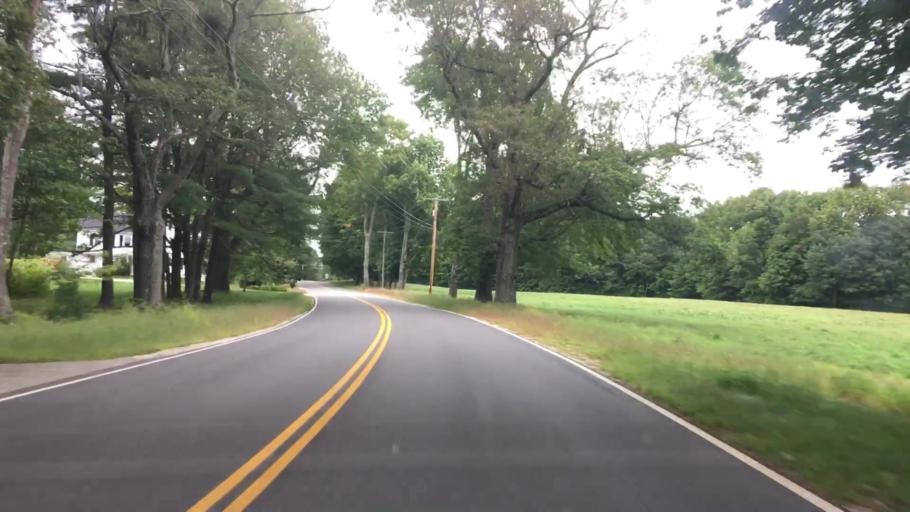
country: US
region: Maine
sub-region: Cumberland County
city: New Gloucester
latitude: 43.9045
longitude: -70.2511
